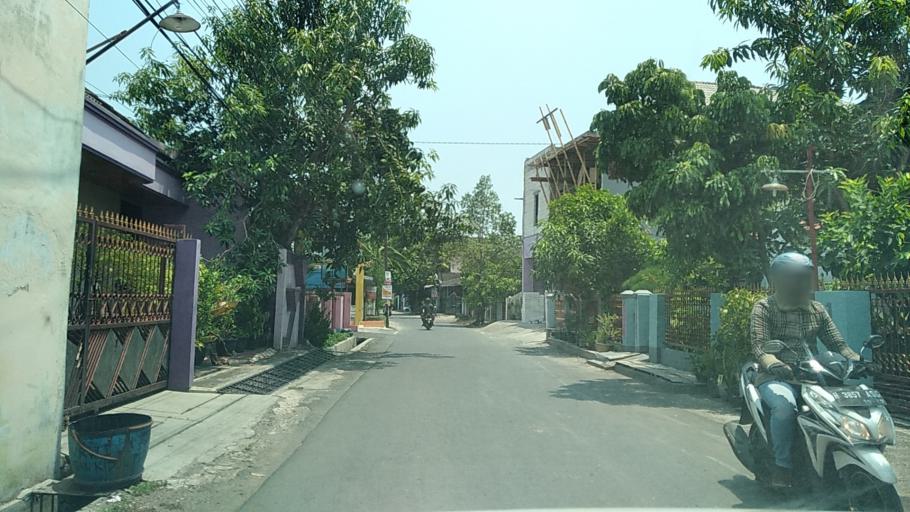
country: ID
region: Central Java
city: Mranggen
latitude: -7.0168
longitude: 110.4732
